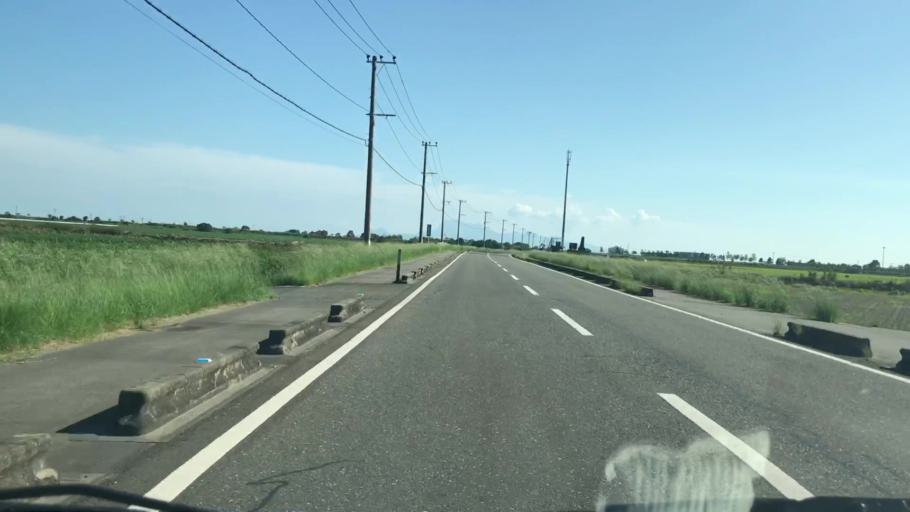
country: JP
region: Saga Prefecture
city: Okawa
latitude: 33.1601
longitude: 130.3087
